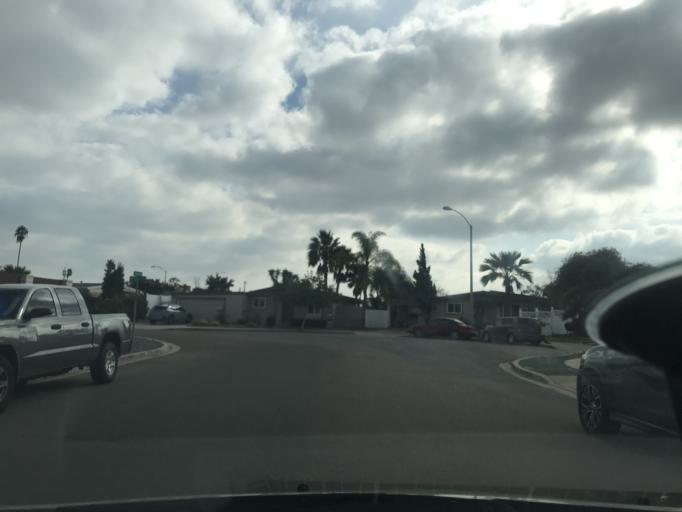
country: US
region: California
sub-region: San Diego County
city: San Diego
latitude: 32.8009
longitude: -117.1368
